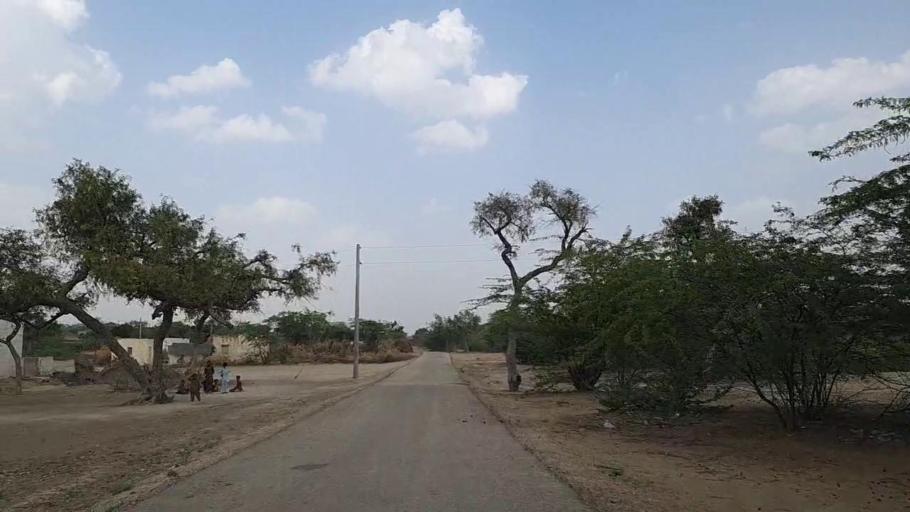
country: PK
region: Sindh
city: Islamkot
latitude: 24.8389
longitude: 70.1433
